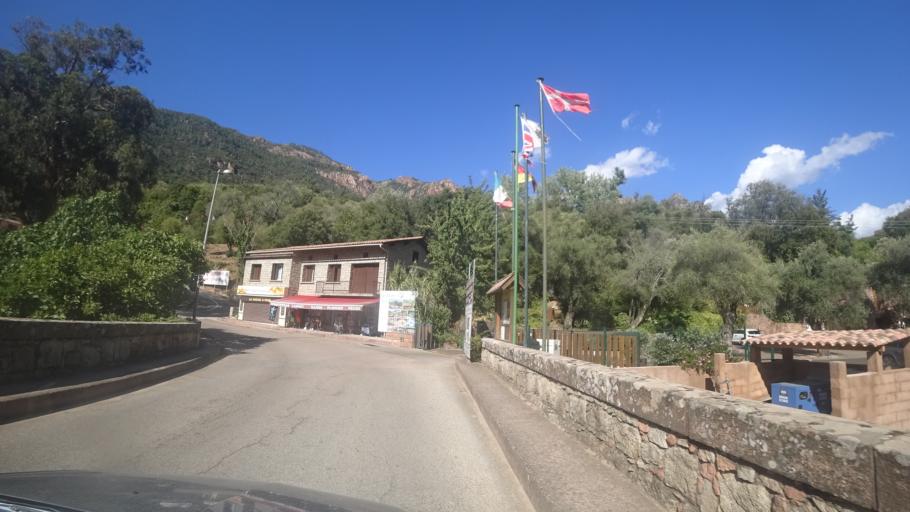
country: FR
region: Corsica
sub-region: Departement de la Corse-du-Sud
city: Cargese
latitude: 42.2620
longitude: 8.7098
